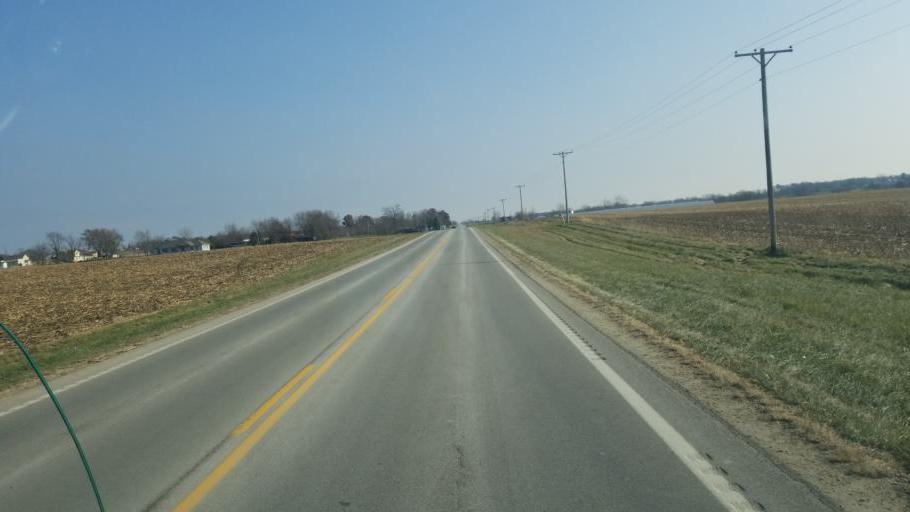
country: US
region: Ohio
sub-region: Mercer County
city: Fort Recovery
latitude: 40.4213
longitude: -84.7438
